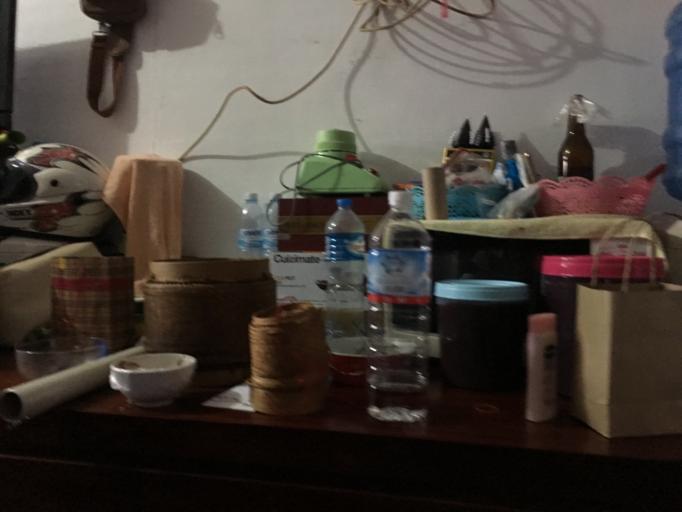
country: LA
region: Vientiane
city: Vientiane
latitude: 17.9938
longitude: 102.6378
